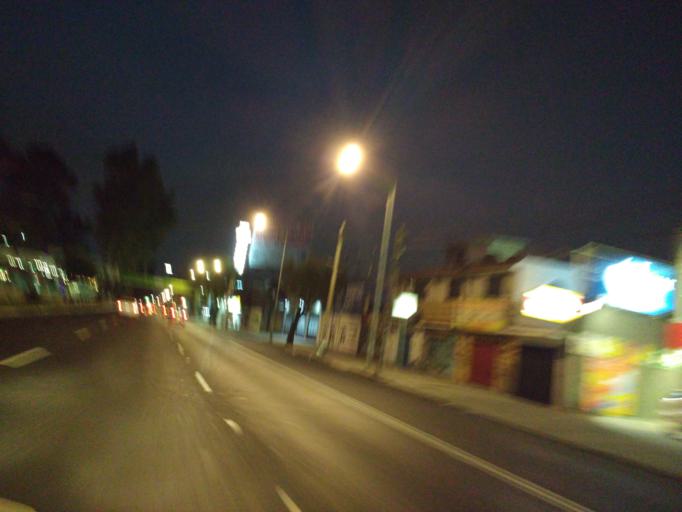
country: MX
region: Mexico City
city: Coyoacan
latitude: 19.3267
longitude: -99.1389
